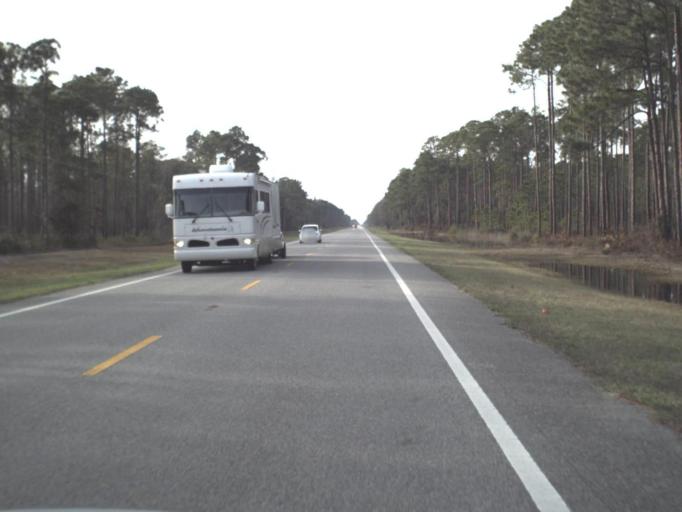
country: US
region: Florida
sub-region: Bay County
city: Mexico Beach
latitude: 30.0042
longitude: -85.5049
